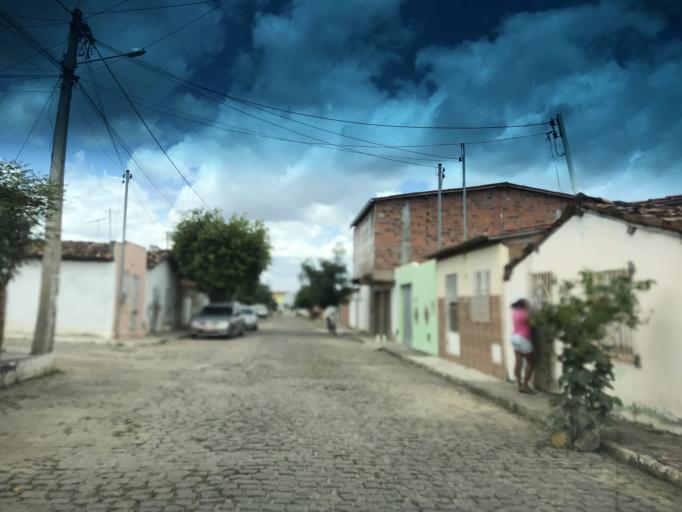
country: BR
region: Bahia
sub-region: Itaberaba
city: Itaberaba
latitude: -12.5355
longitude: -40.3036
